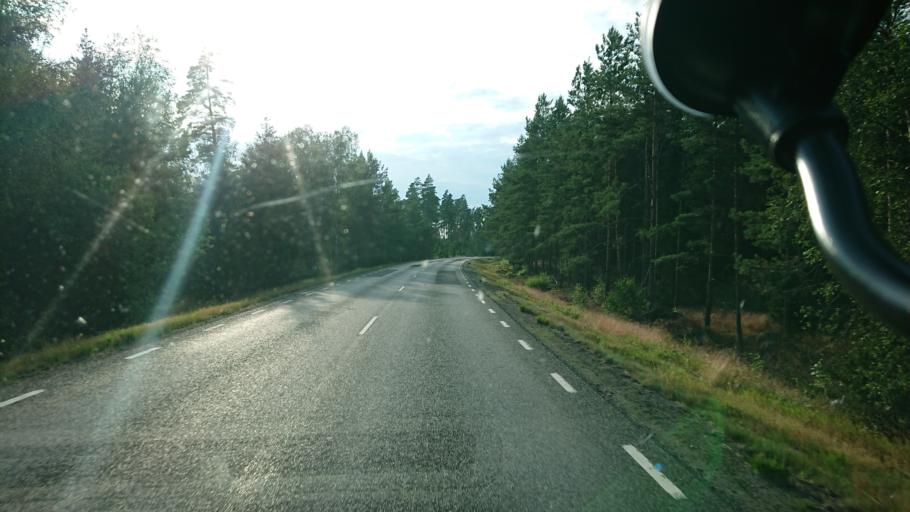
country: SE
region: Kronoberg
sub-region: Vaxjo Kommun
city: Braas
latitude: 57.0263
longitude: 14.9814
